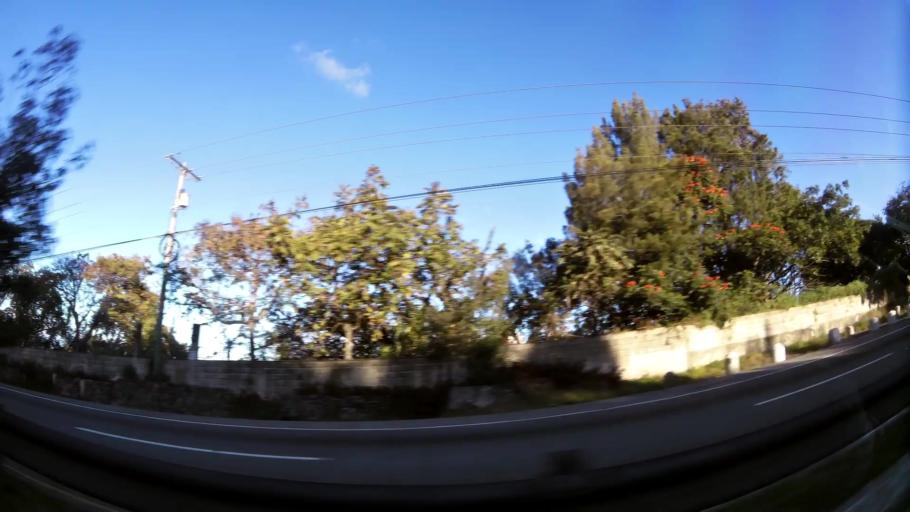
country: GT
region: Guatemala
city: Mixco
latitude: 14.6158
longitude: -90.6169
